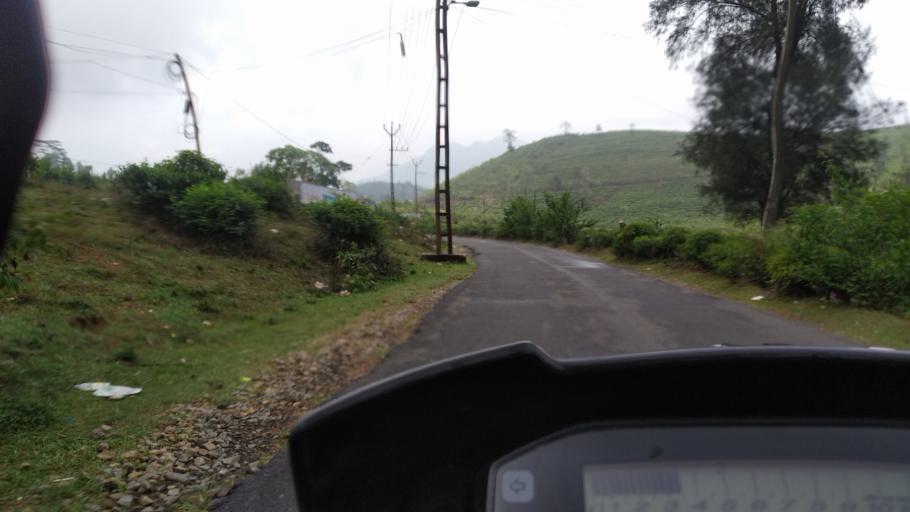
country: IN
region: Kerala
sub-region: Kottayam
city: Erattupetta
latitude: 9.6353
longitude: 76.9501
